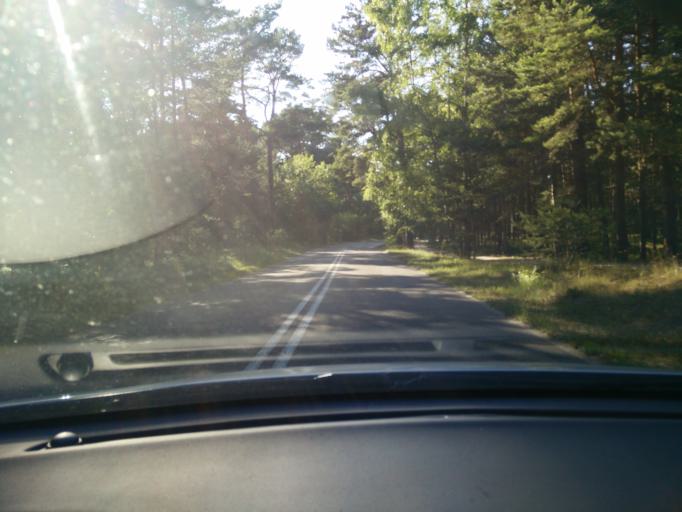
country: PL
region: Pomeranian Voivodeship
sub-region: Powiat pucki
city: Jastarnia
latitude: 54.6712
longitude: 18.7340
